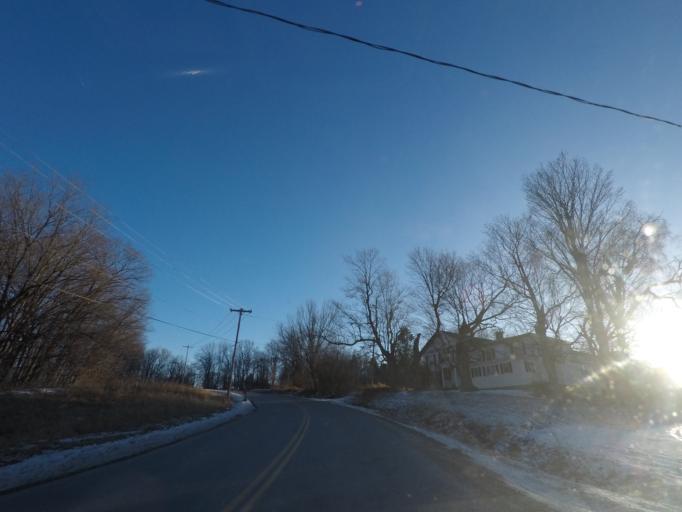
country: US
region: New York
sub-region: Rensselaer County
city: Poestenkill
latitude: 42.7016
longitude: -73.5816
